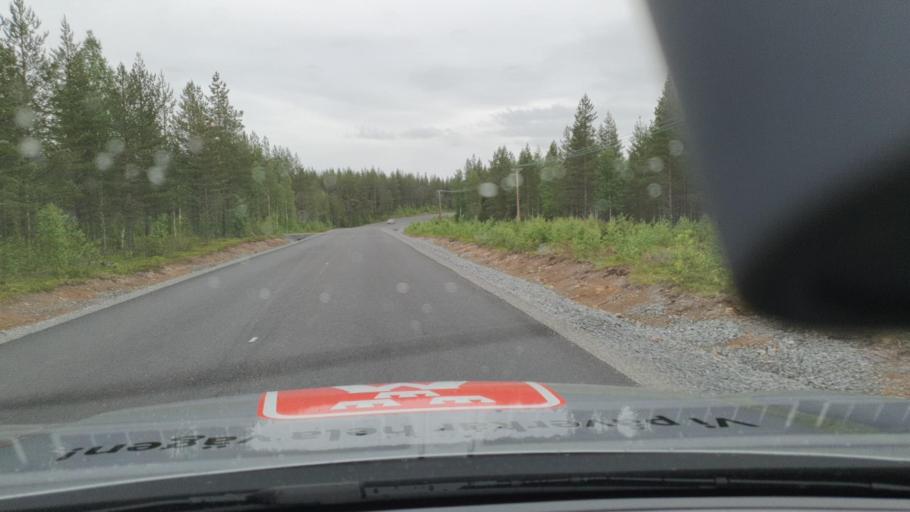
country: SE
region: Norrbotten
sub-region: Overkalix Kommun
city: OEverkalix
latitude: 66.6717
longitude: 23.2213
